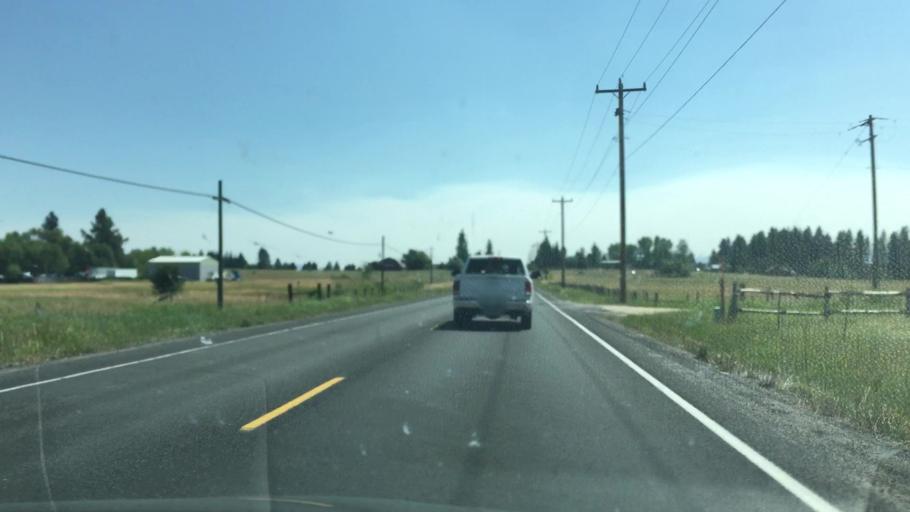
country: US
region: Idaho
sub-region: Valley County
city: McCall
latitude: 44.8765
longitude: -116.0908
